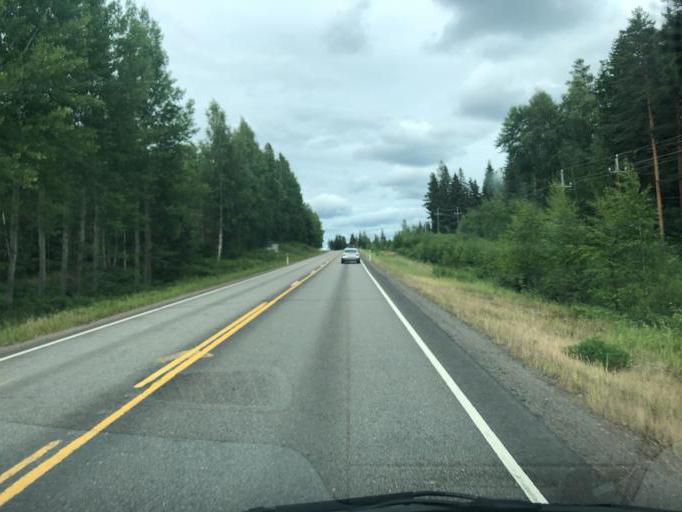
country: FI
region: Kymenlaakso
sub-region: Kouvola
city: Kouvola
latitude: 60.9712
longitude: 26.8955
